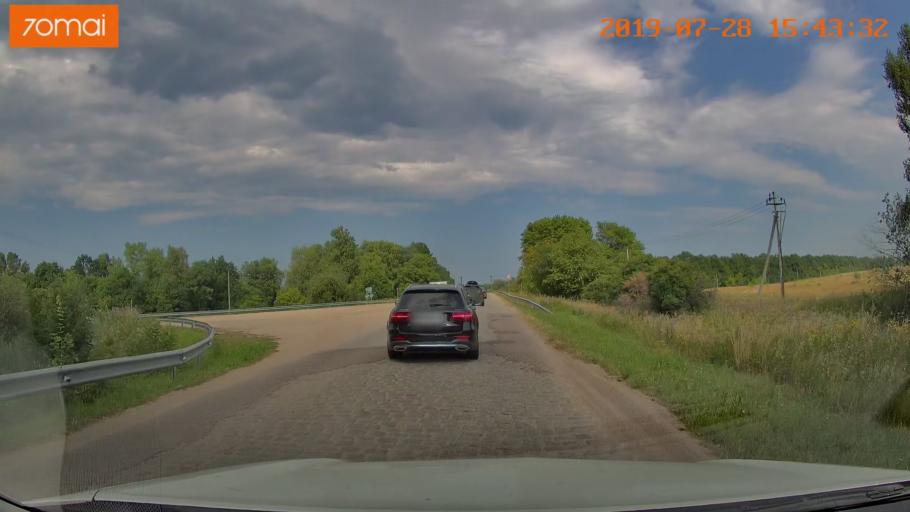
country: RU
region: Kaliningrad
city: Donskoye
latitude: 54.9377
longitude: 20.0256
